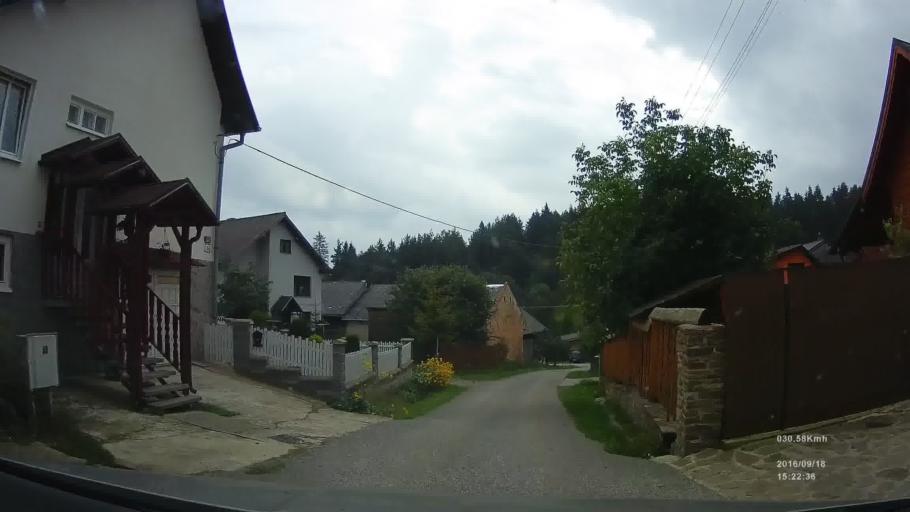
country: SK
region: Presovsky
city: Lubica
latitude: 49.0419
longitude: 20.4874
